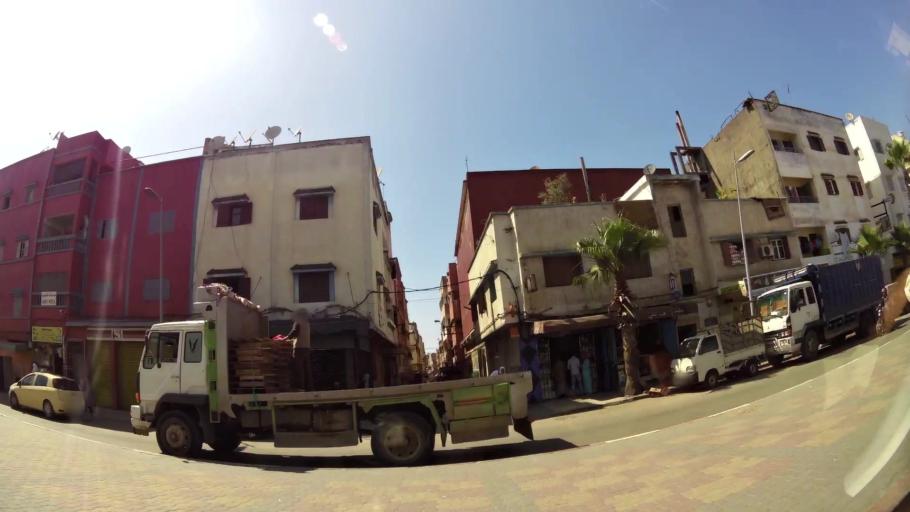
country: MA
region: Rabat-Sale-Zemmour-Zaer
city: Sale
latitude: 34.0628
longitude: -6.7714
